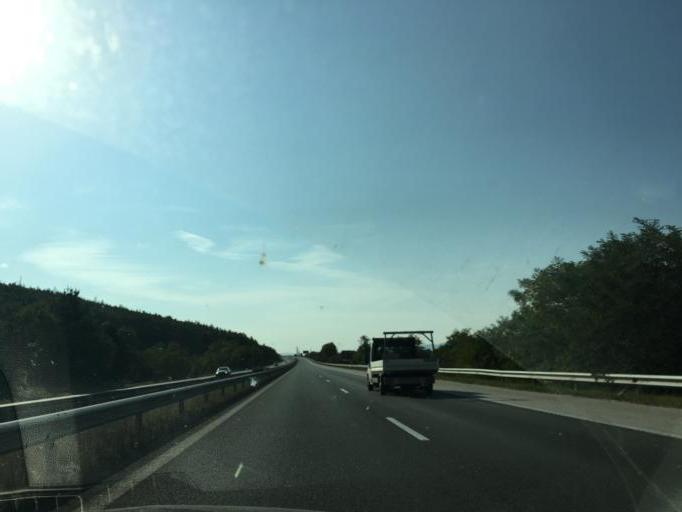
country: BG
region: Sofiya
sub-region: Obshtina Ikhtiman
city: Ikhtiman
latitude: 42.4999
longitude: 23.7715
